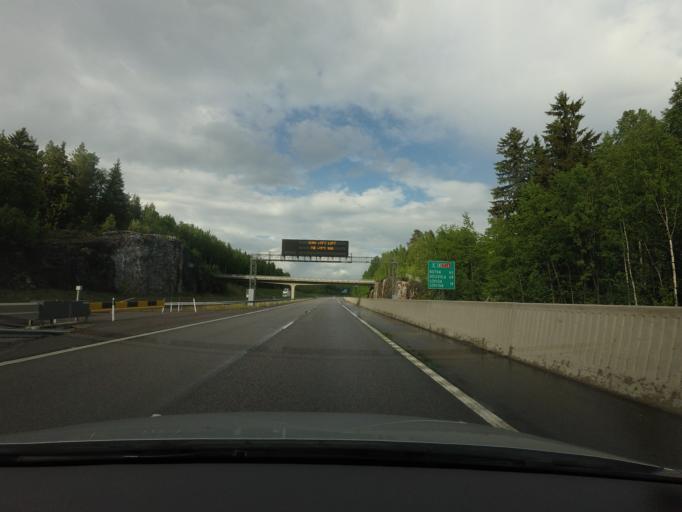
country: FI
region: Uusimaa
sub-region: Loviisa
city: Perna
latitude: 60.4907
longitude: 25.9148
